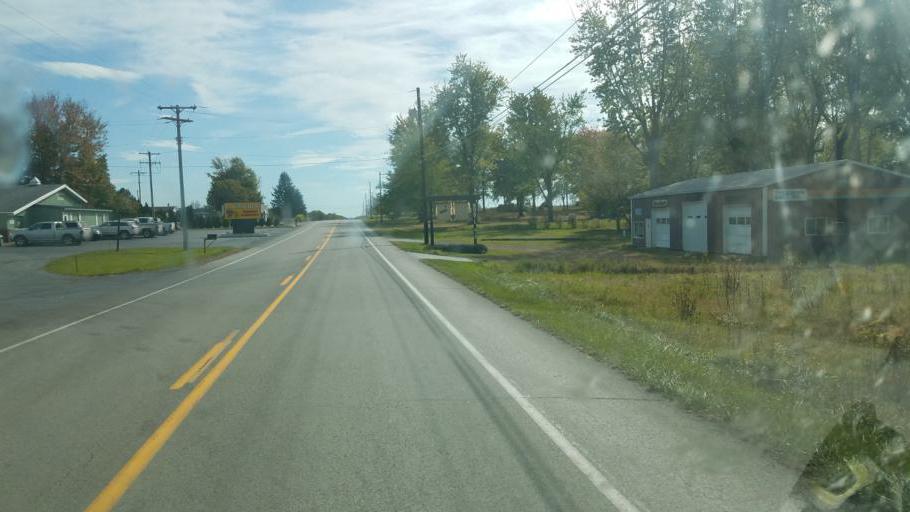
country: US
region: Pennsylvania
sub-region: Mercer County
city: Mercer
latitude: 41.3212
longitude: -80.2312
